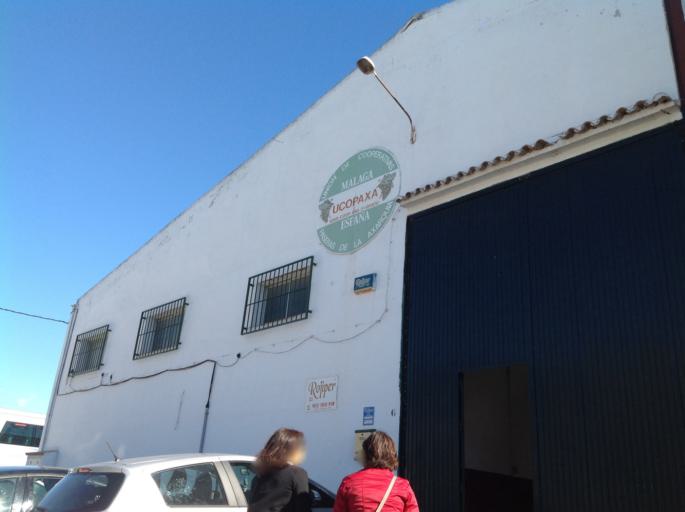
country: ES
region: Andalusia
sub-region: Provincia de Malaga
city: Velez-Malaga
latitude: 36.7663
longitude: -4.0926
